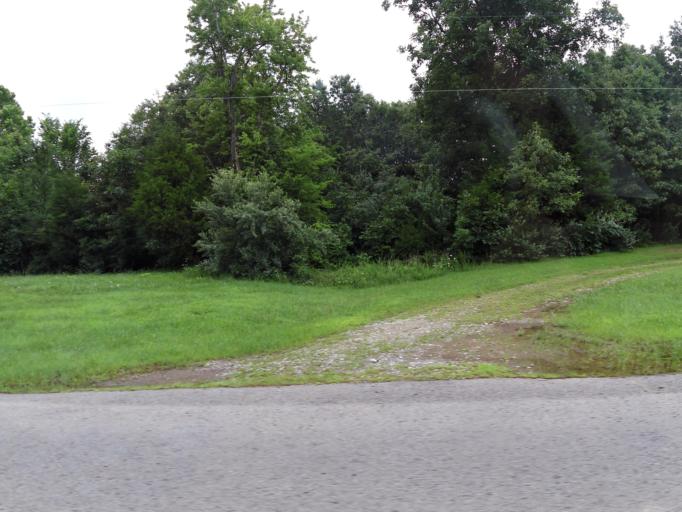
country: US
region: Kentucky
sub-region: Hopkins County
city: Madisonville
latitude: 37.3240
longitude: -87.3751
